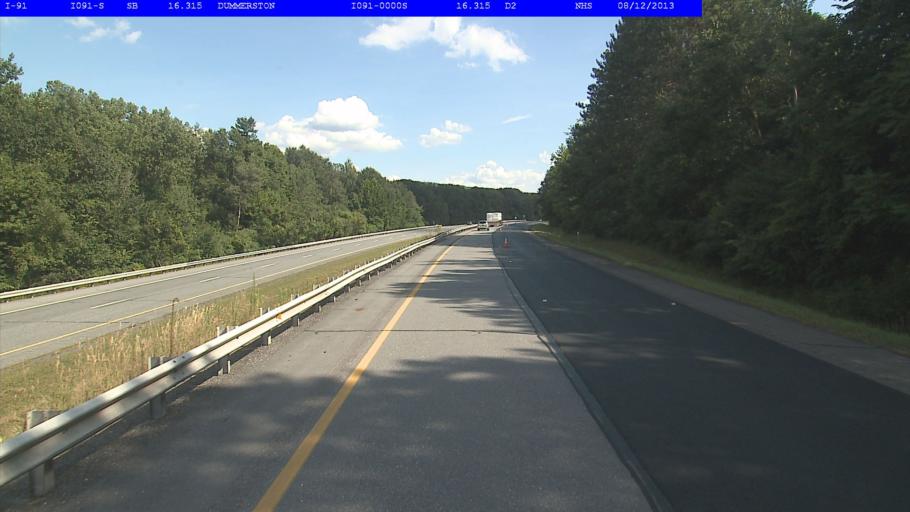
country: US
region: New Hampshire
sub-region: Cheshire County
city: Chesterfield
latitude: 42.9446
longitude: -72.5307
